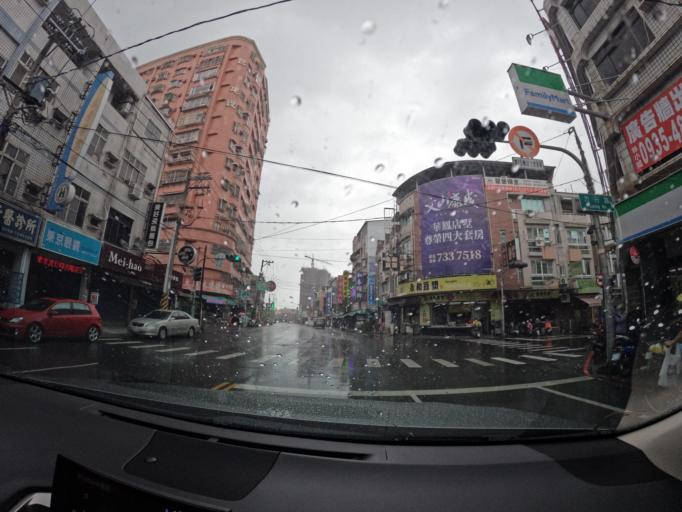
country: TW
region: Taiwan
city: Fengshan
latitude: 22.6391
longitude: 120.3647
